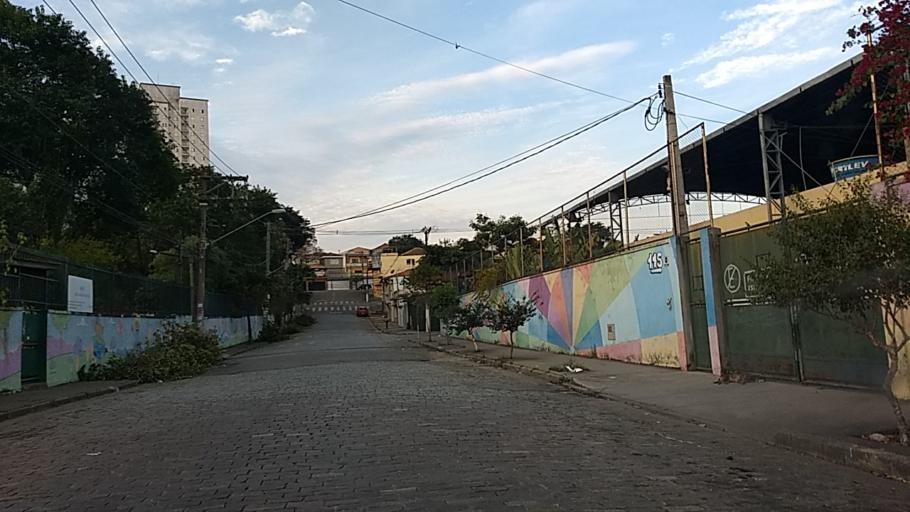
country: BR
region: Sao Paulo
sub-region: Guarulhos
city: Guarulhos
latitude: -23.5103
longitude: -46.5761
